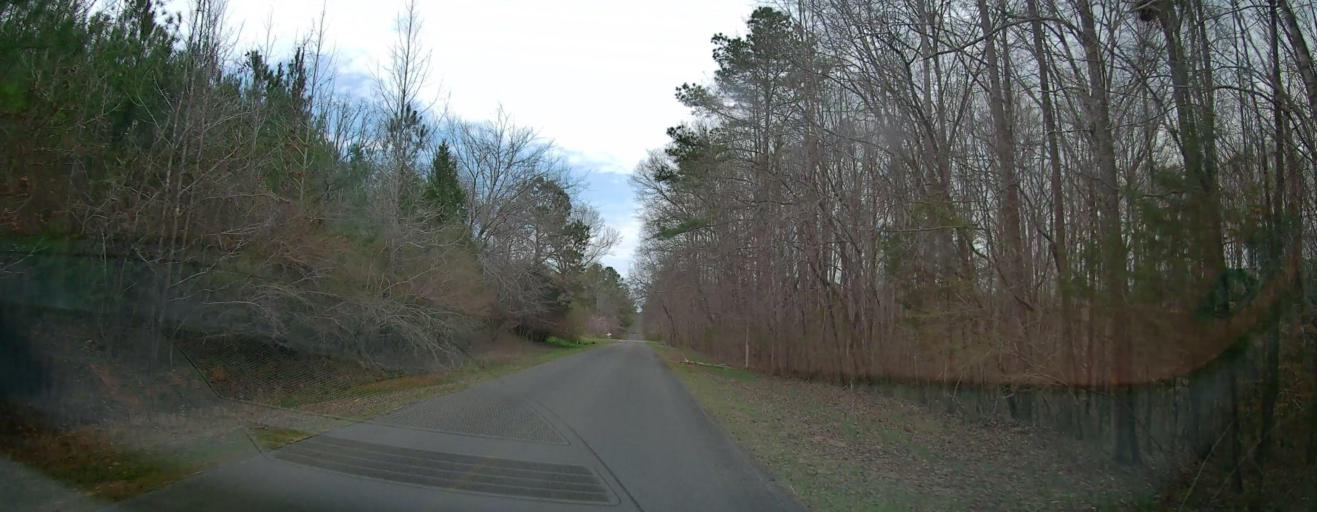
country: US
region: Alabama
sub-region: Marion County
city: Hamilton
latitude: 34.1992
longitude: -88.1830
